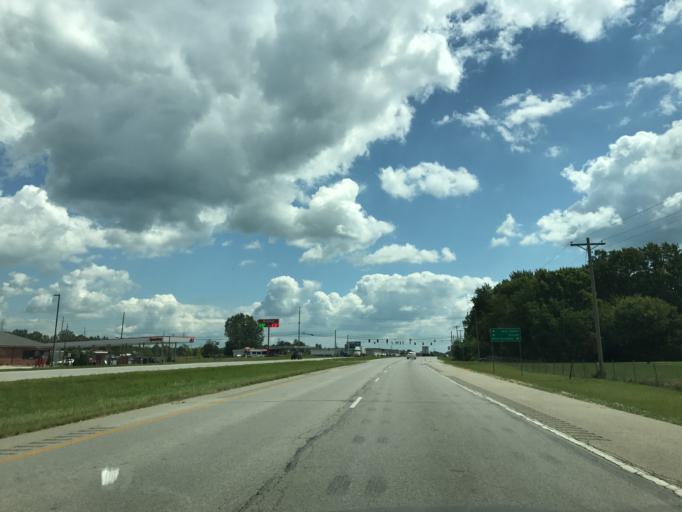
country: US
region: Indiana
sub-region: Kosciusko County
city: Pierceton
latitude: 41.2054
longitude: -85.7086
